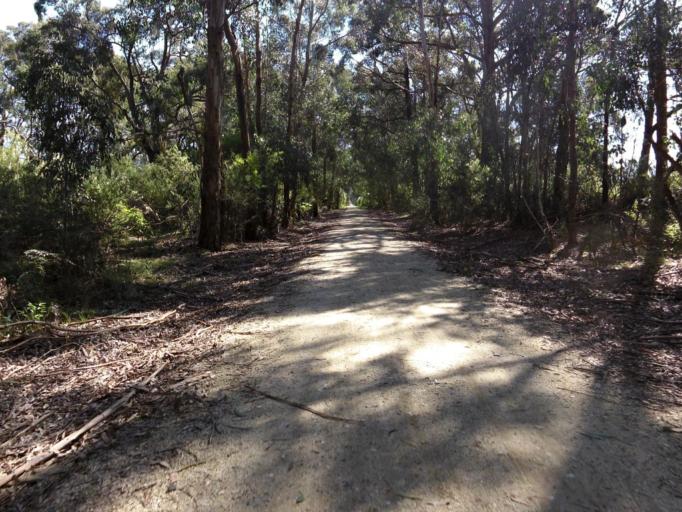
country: AU
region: Victoria
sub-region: Latrobe
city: Morwell
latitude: -38.6650
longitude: 146.2536
